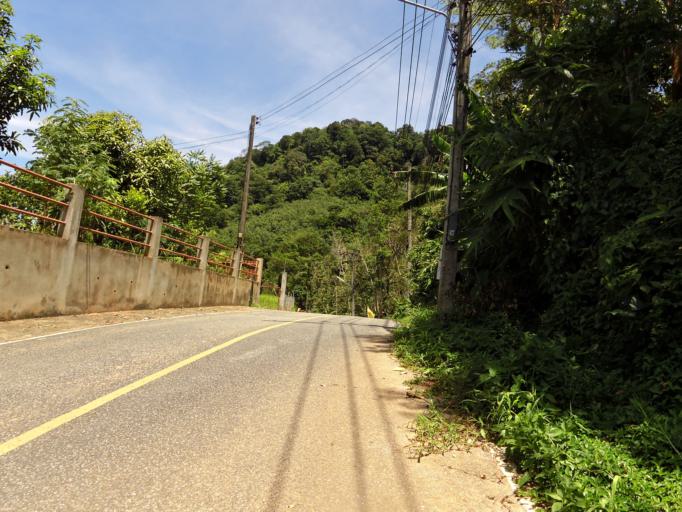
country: TH
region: Phuket
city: Ban Karon
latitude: 7.8502
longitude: 98.3068
